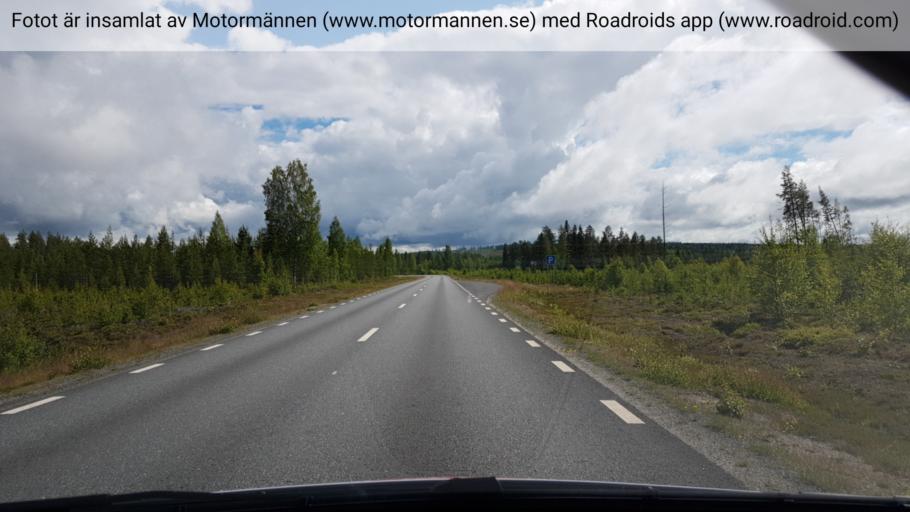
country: SE
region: Vaesterbotten
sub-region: Bjurholms Kommun
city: Bjurholm
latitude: 64.2981
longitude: 19.1766
